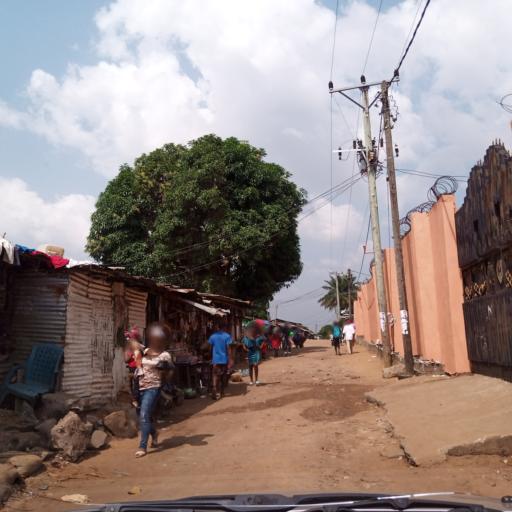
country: LR
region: Montserrado
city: Monrovia
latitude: 6.2917
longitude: -10.7659
